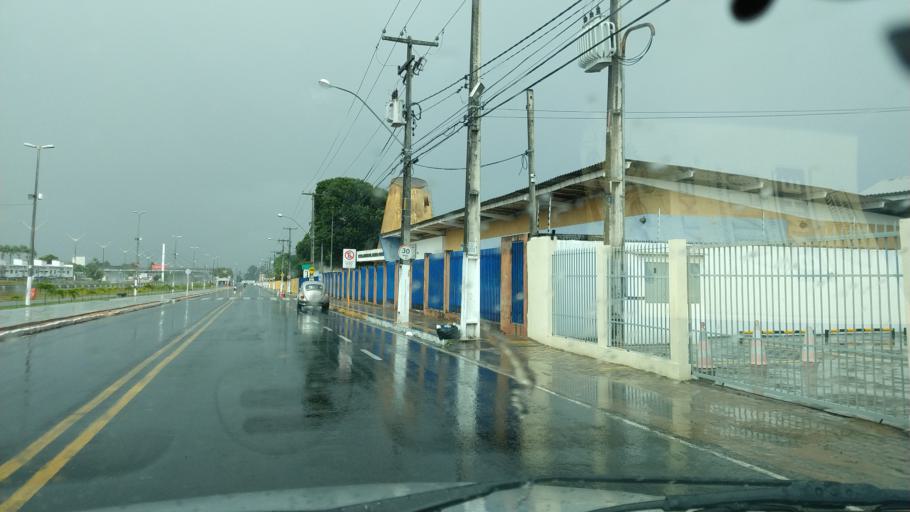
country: BR
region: Rio Grande do Norte
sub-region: Parnamirim
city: Parnamirim
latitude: -5.9237
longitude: -35.2652
